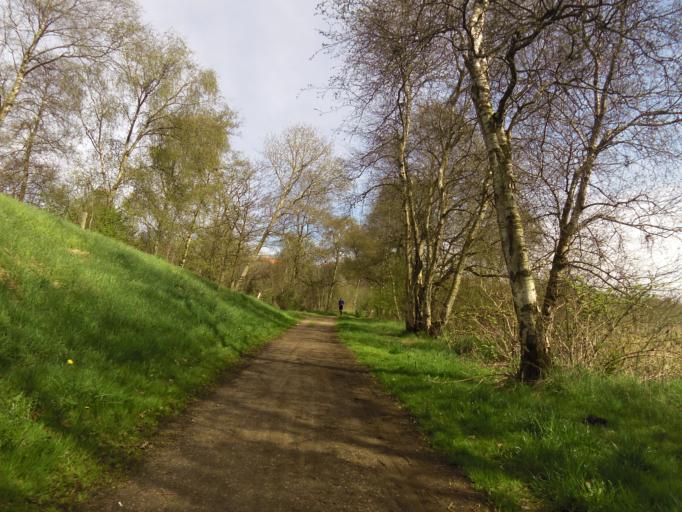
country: DK
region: Central Jutland
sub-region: Skive Kommune
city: Skive
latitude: 56.5666
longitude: 9.0119
